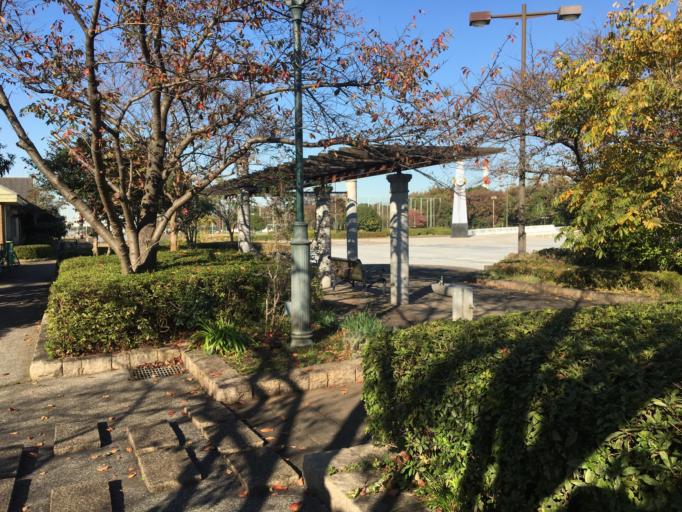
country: JP
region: Tokyo
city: Urayasu
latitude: 35.6497
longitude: 139.8236
